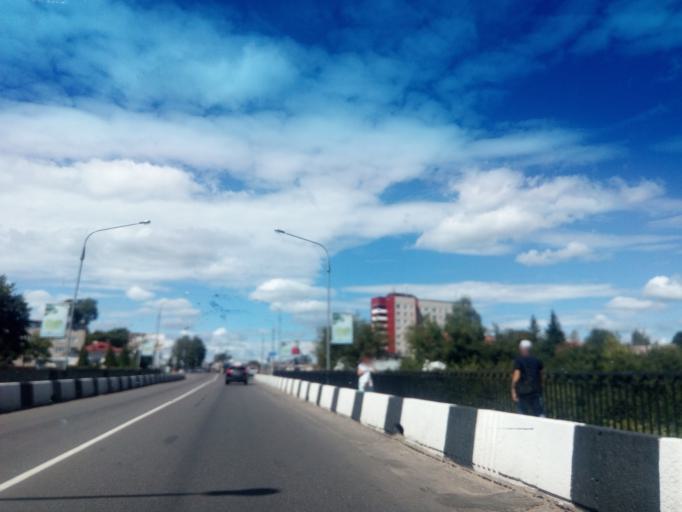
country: BY
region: Vitebsk
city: Polatsk
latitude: 55.4936
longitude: 28.7714
